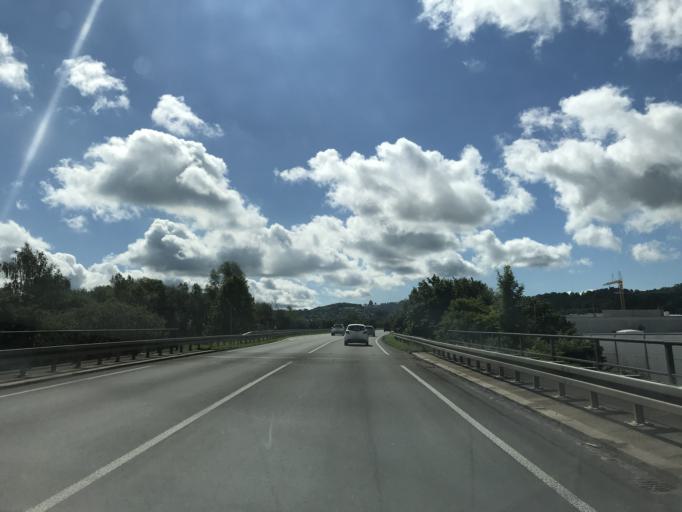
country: DE
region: Baden-Wuerttemberg
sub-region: Freiburg Region
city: Maulburg
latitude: 47.6478
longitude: 7.7913
